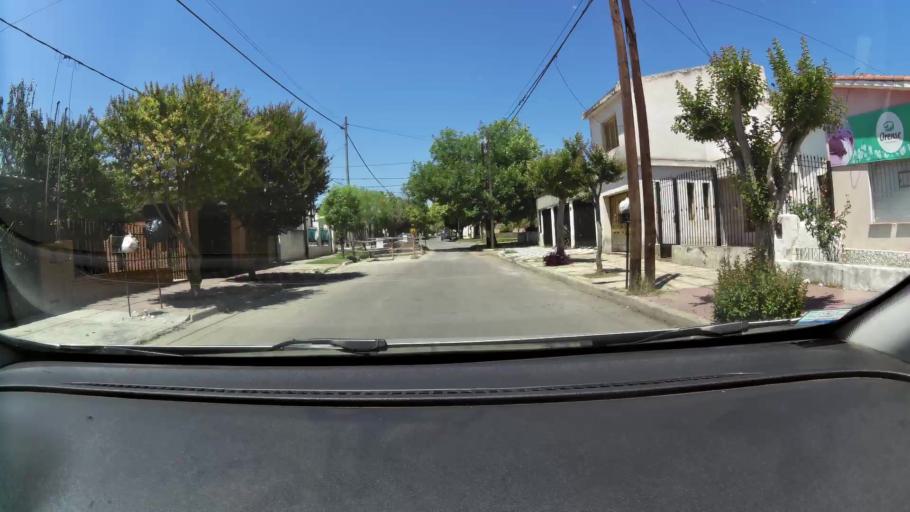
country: AR
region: Cordoba
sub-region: Departamento de Capital
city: Cordoba
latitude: -31.4147
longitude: -64.2145
